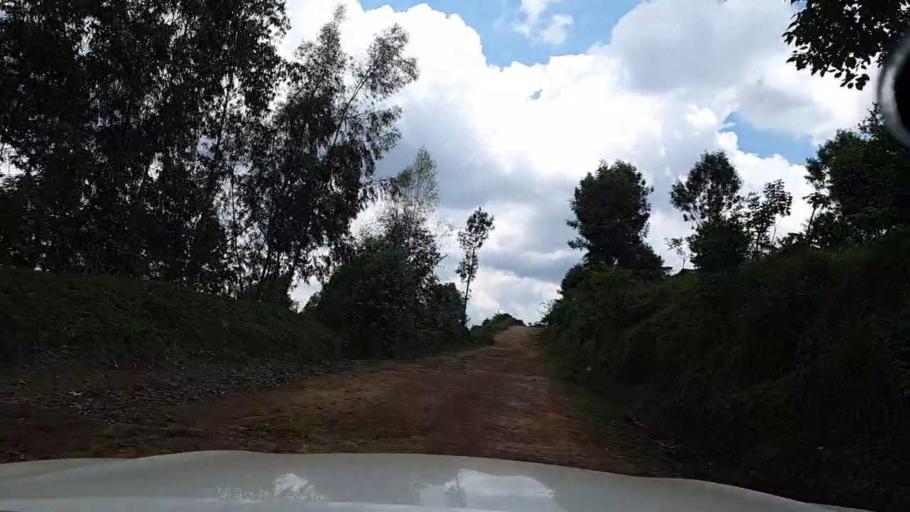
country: RW
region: Southern Province
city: Nzega
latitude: -2.6363
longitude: 29.4889
